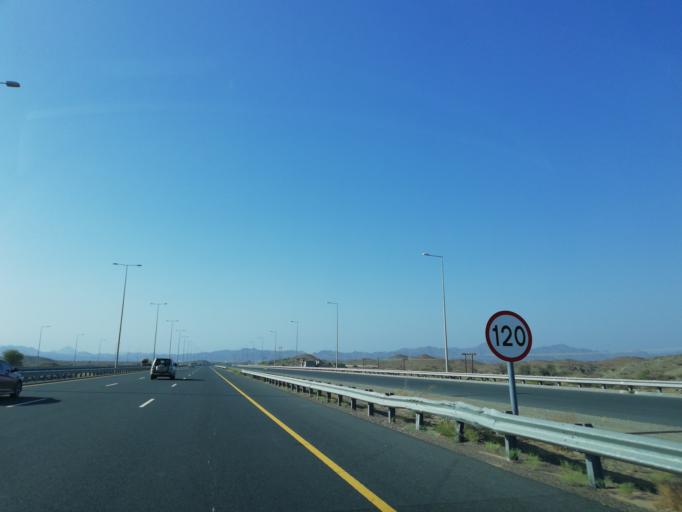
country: OM
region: Muhafazat ad Dakhiliyah
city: Sufalat Sama'il
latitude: 23.0780
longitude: 58.1849
